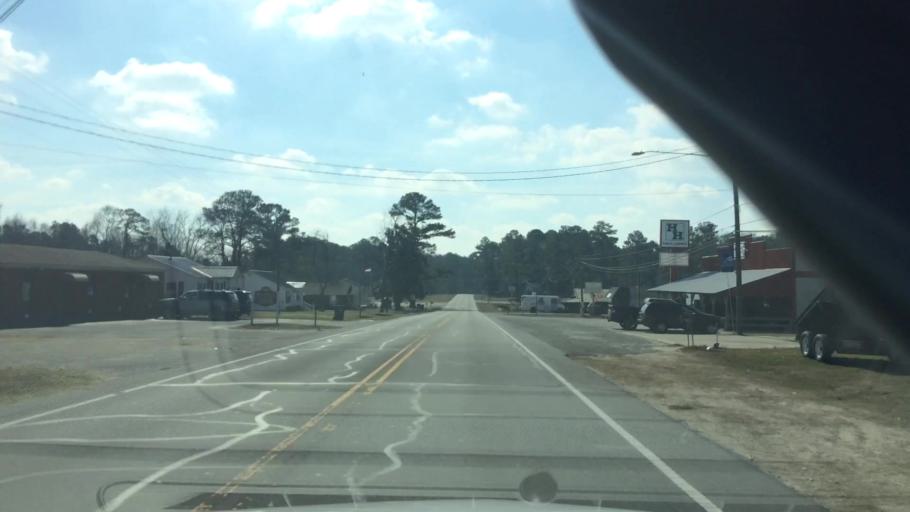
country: US
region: North Carolina
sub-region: Duplin County
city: Beulaville
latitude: 35.0634
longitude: -77.7395
